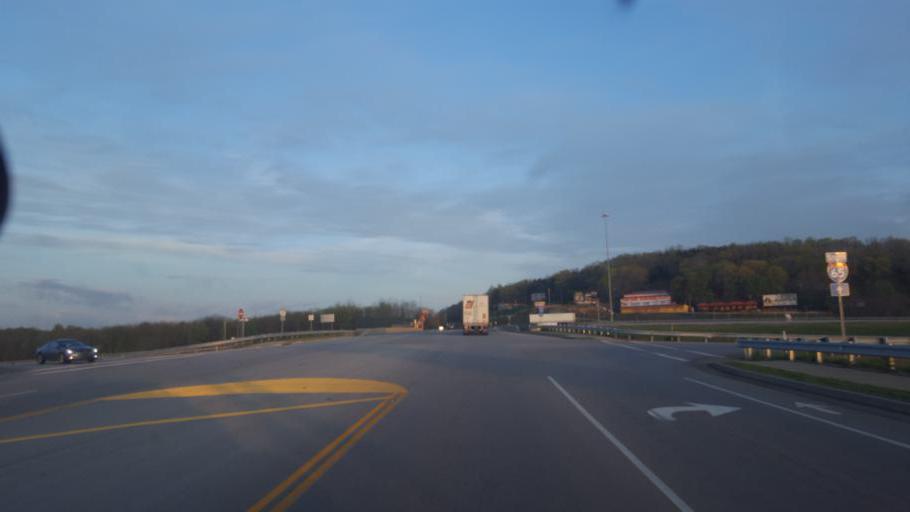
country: US
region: Kentucky
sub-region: Barren County
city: Cave City
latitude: 37.1352
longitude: -85.9765
